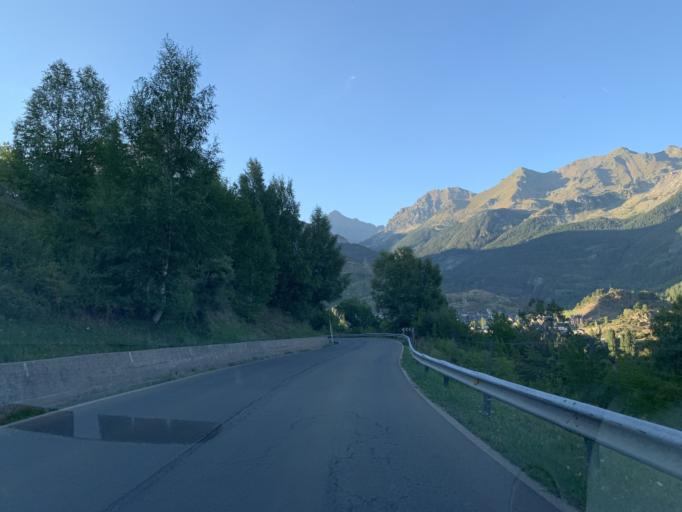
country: ES
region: Aragon
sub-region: Provincia de Huesca
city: Sallent de Gallego
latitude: 42.7631
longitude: -0.3359
